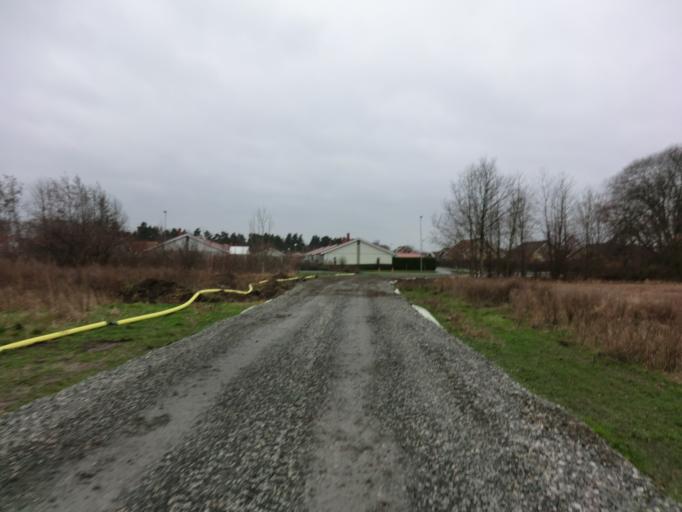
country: SE
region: Skane
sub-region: Eslovs Kommun
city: Eslov
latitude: 55.7242
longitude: 13.3557
